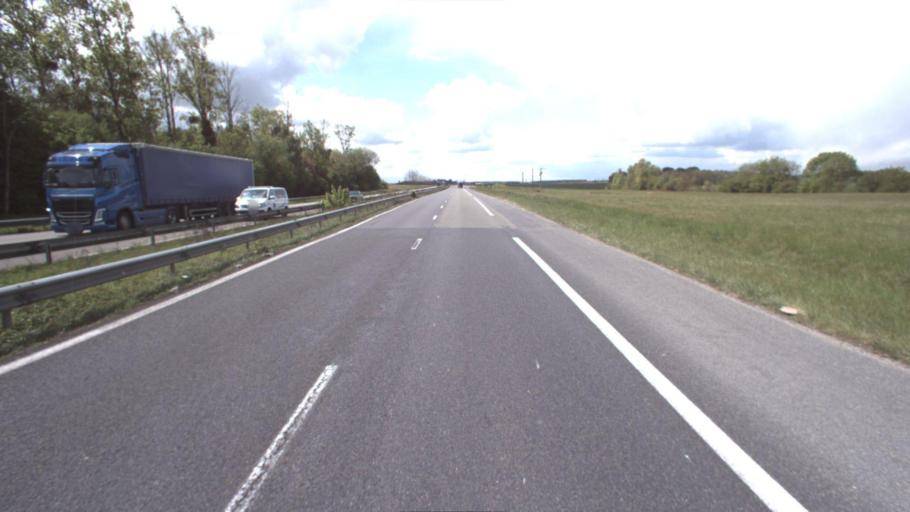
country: FR
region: Ile-de-France
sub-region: Departement de Seine-et-Marne
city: Rozay-en-Brie
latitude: 48.6860
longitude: 3.0064
